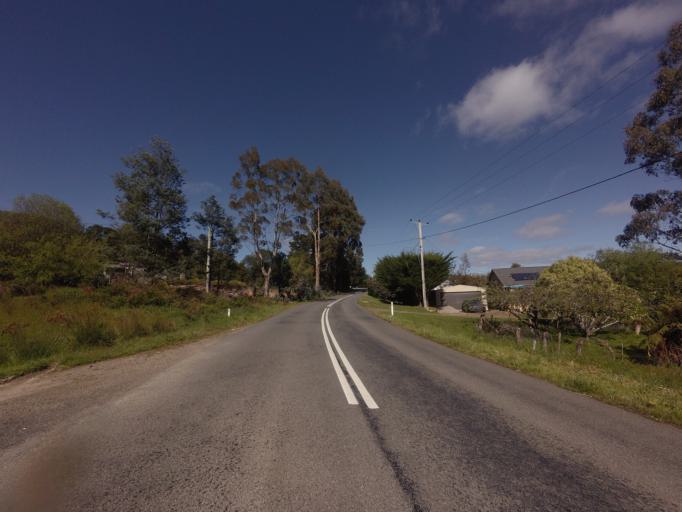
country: AU
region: Tasmania
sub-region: Derwent Valley
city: New Norfolk
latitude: -42.7482
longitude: 146.6486
